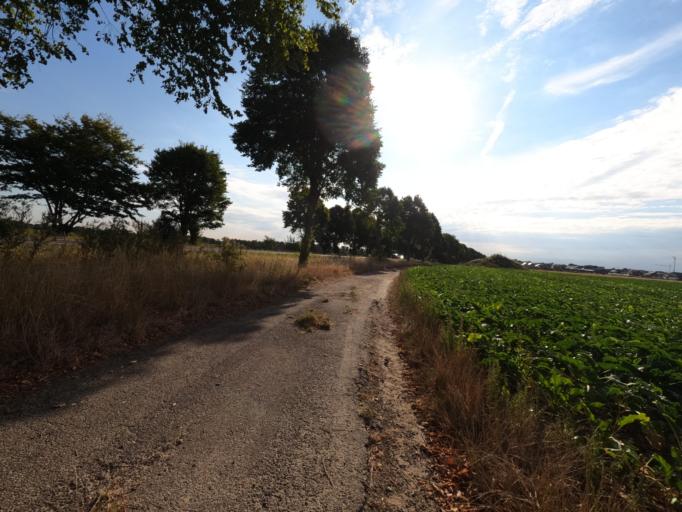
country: DE
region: North Rhine-Westphalia
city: Erkelenz
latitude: 51.0887
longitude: 6.2871
